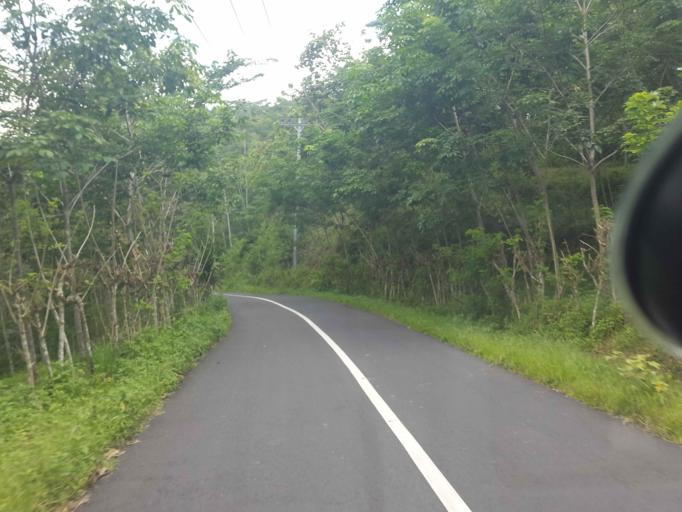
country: ID
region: Central Java
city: Sudikampir
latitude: -7.4210
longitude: 108.9745
